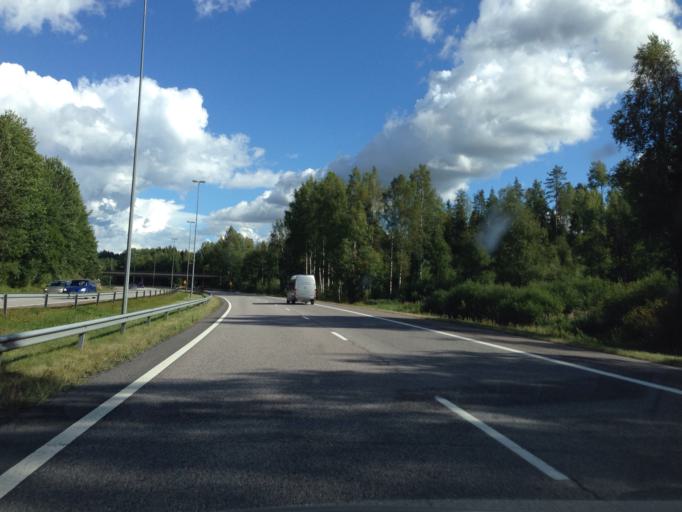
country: FI
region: Uusimaa
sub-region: Helsinki
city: Vihti
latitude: 60.2919
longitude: 24.3251
